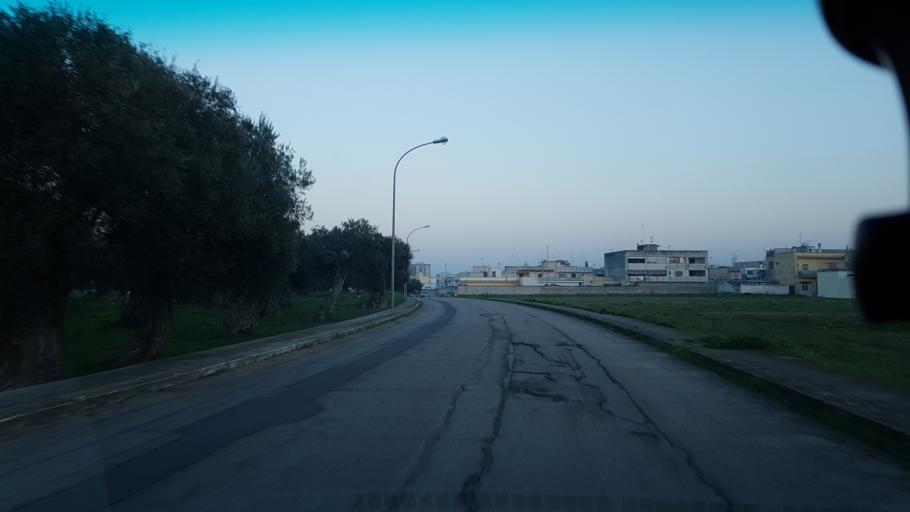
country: IT
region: Apulia
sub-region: Provincia di Brindisi
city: Mesagne
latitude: 40.5639
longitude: 17.7937
